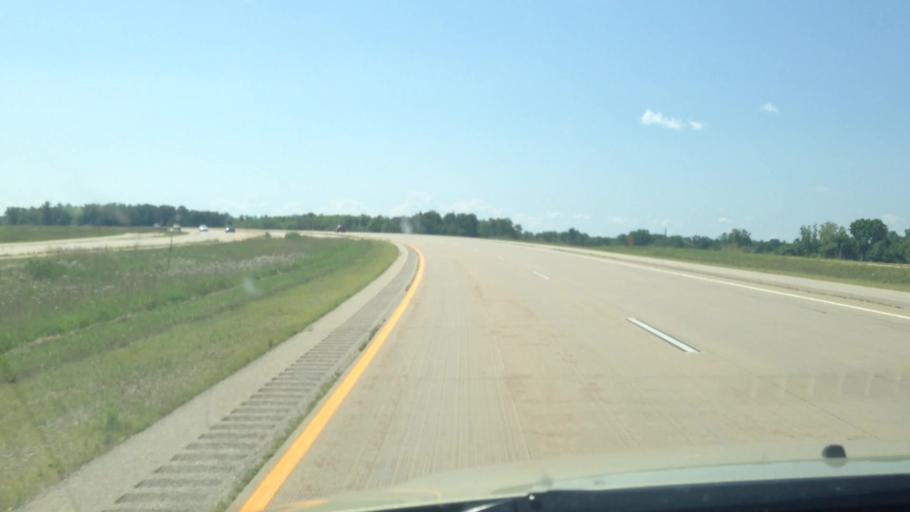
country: US
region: Wisconsin
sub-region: Oconto County
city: Oconto
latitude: 44.8974
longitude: -87.9000
